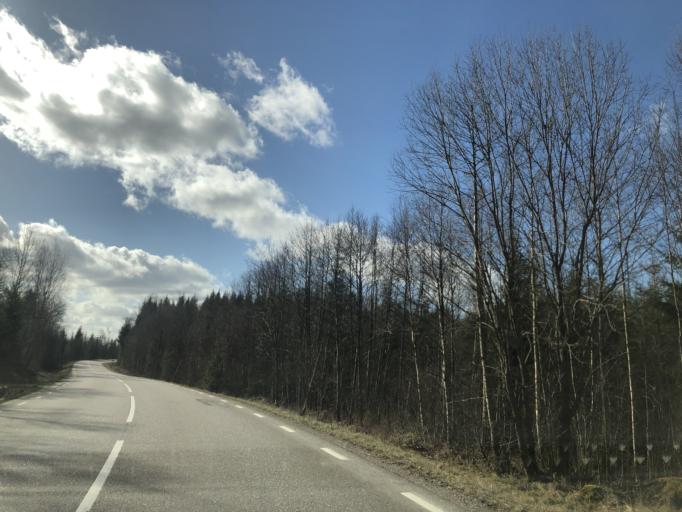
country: SE
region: Vaestra Goetaland
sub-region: Ulricehamns Kommun
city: Ulricehamn
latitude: 57.6666
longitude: 13.4163
